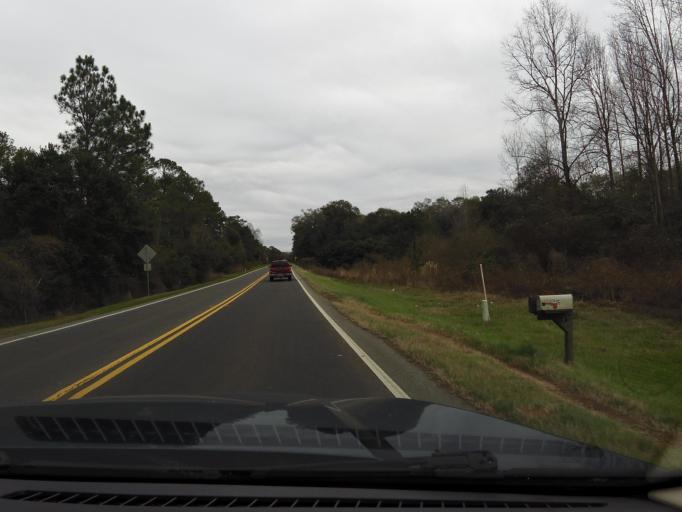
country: US
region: Georgia
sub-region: Randolph County
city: Shellman
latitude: 31.7820
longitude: -84.6002
